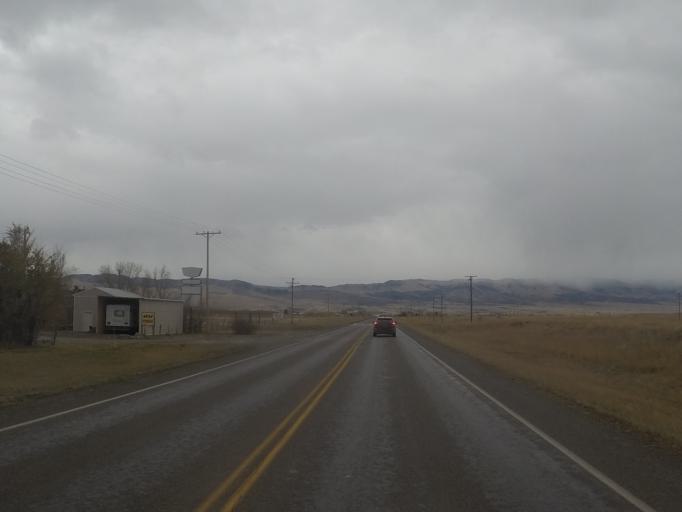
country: US
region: Montana
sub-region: Broadwater County
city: Townsend
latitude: 46.3221
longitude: -111.4812
